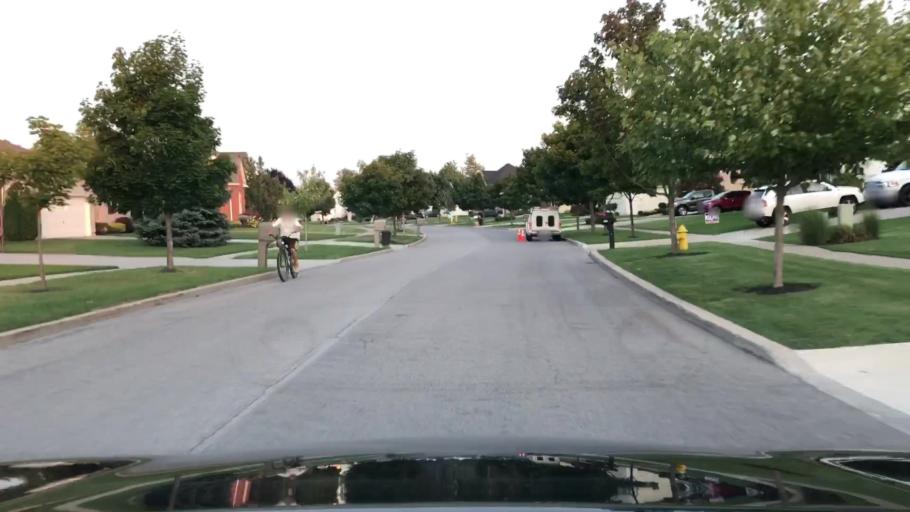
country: US
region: New York
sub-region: Erie County
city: Lancaster
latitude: 42.8669
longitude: -78.6859
